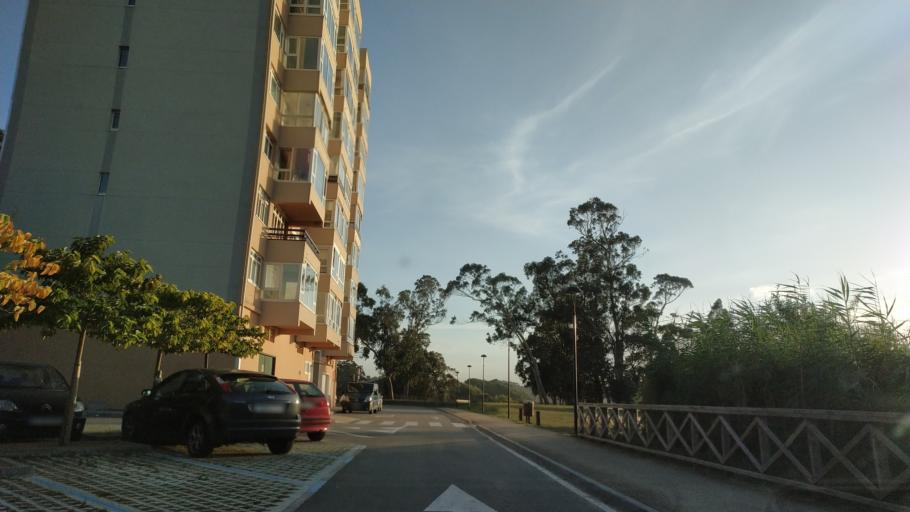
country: ES
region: Galicia
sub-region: Provincia da Coruna
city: Oleiros
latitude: 43.3520
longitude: -8.3473
